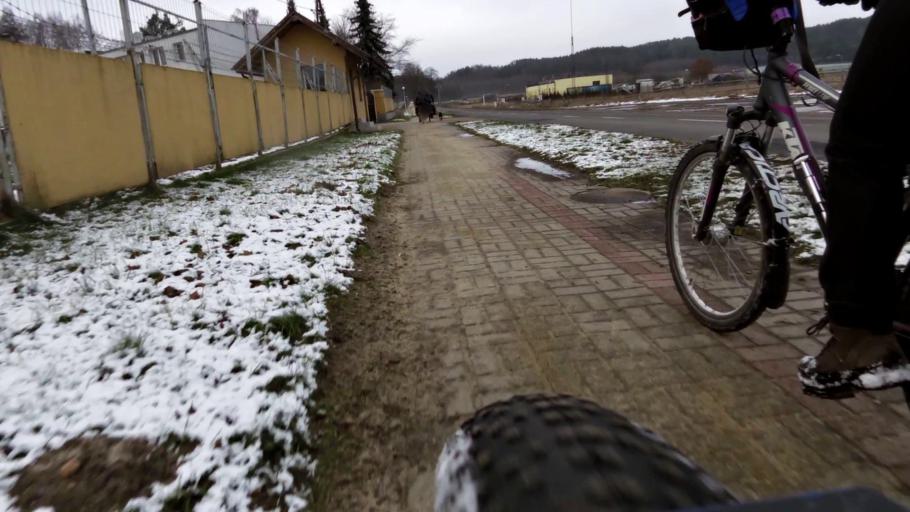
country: PL
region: West Pomeranian Voivodeship
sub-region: Powiat walecki
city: Miroslawiec
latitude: 53.3502
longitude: 16.0864
